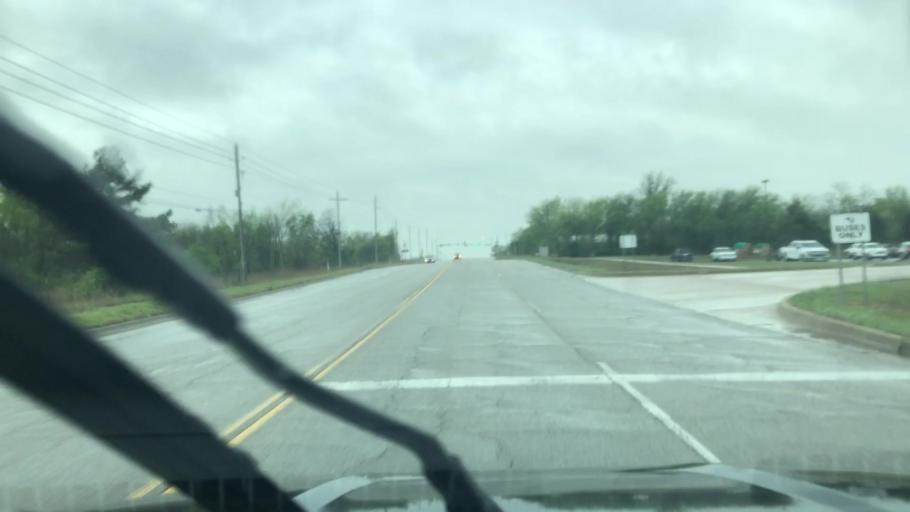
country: US
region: Oklahoma
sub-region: Tulsa County
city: Owasso
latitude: 36.2641
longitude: -95.8868
